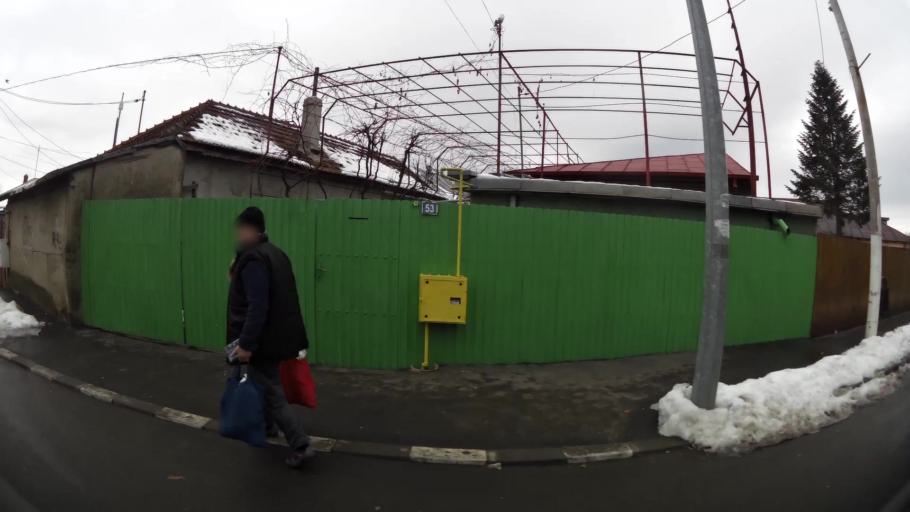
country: RO
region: Ilfov
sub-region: Comuna Pantelimon
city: Pantelimon
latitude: 44.4471
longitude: 26.1991
